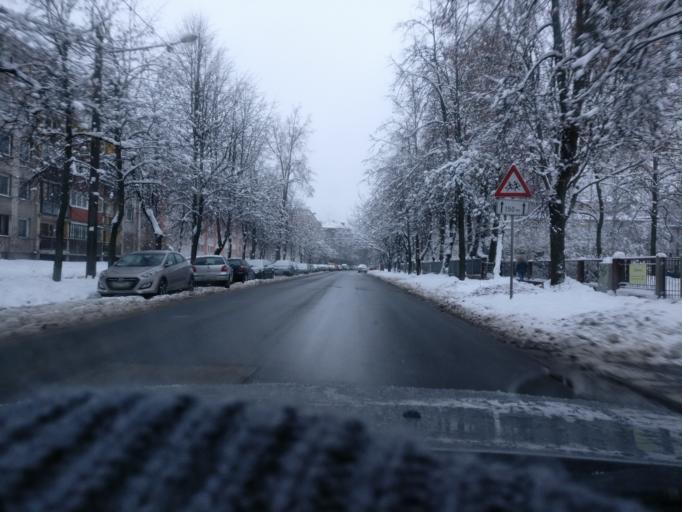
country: LV
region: Marupe
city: Marupe
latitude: 56.9303
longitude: 24.0742
